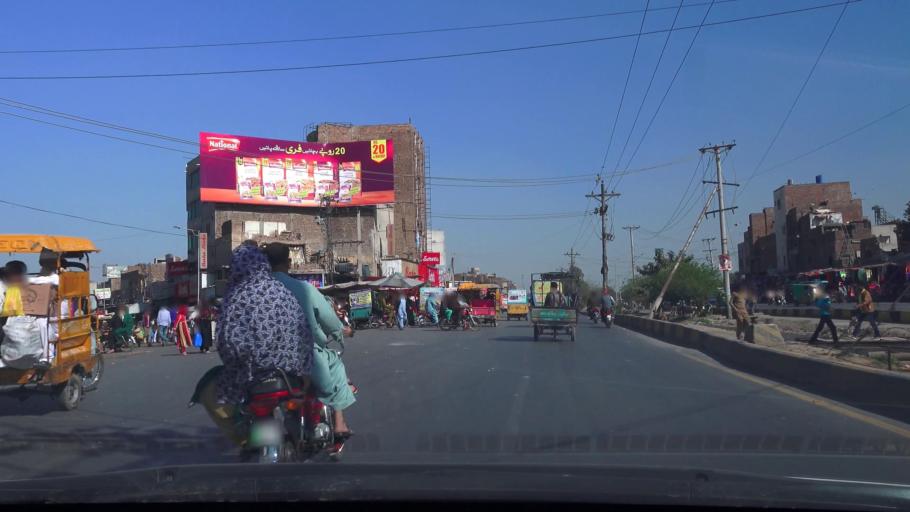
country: PK
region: Punjab
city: Faisalabad
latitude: 31.4138
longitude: 73.0709
